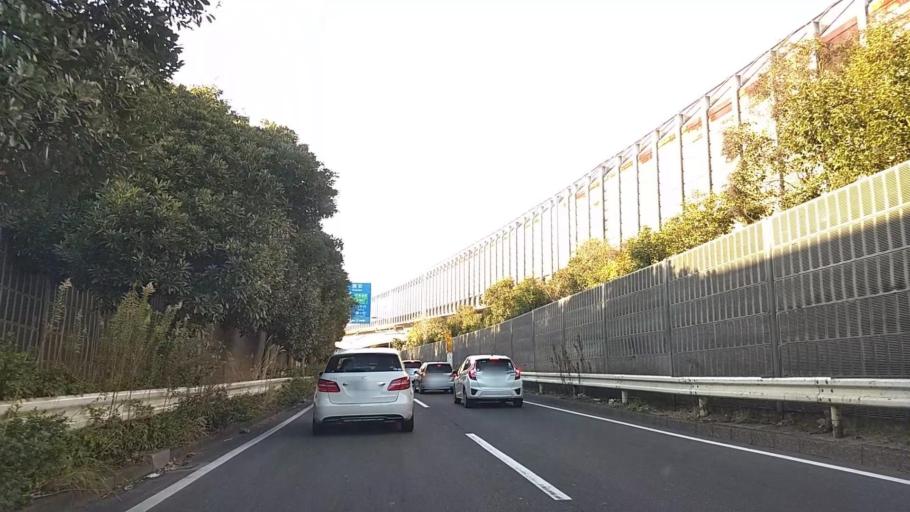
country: JP
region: Chiba
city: Funabashi
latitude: 35.6795
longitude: 140.0005
